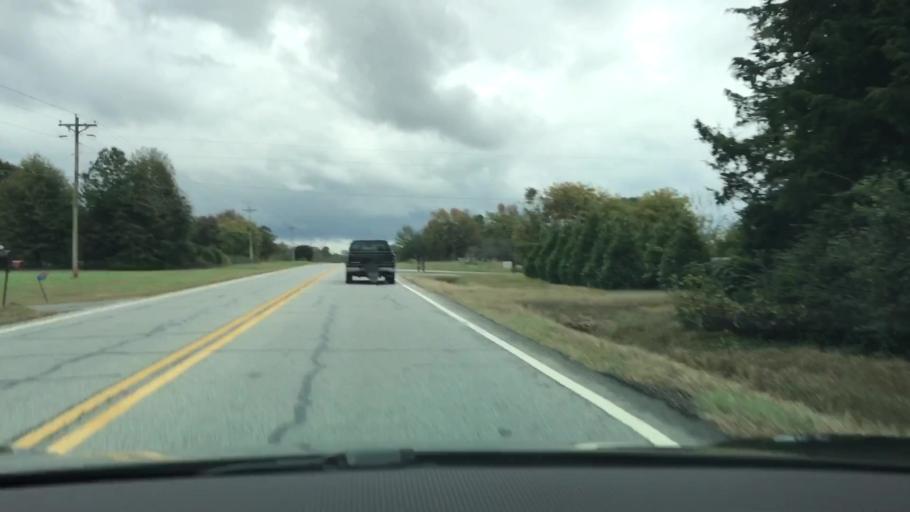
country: US
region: Georgia
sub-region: Oconee County
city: Watkinsville
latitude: 33.8310
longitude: -83.3775
